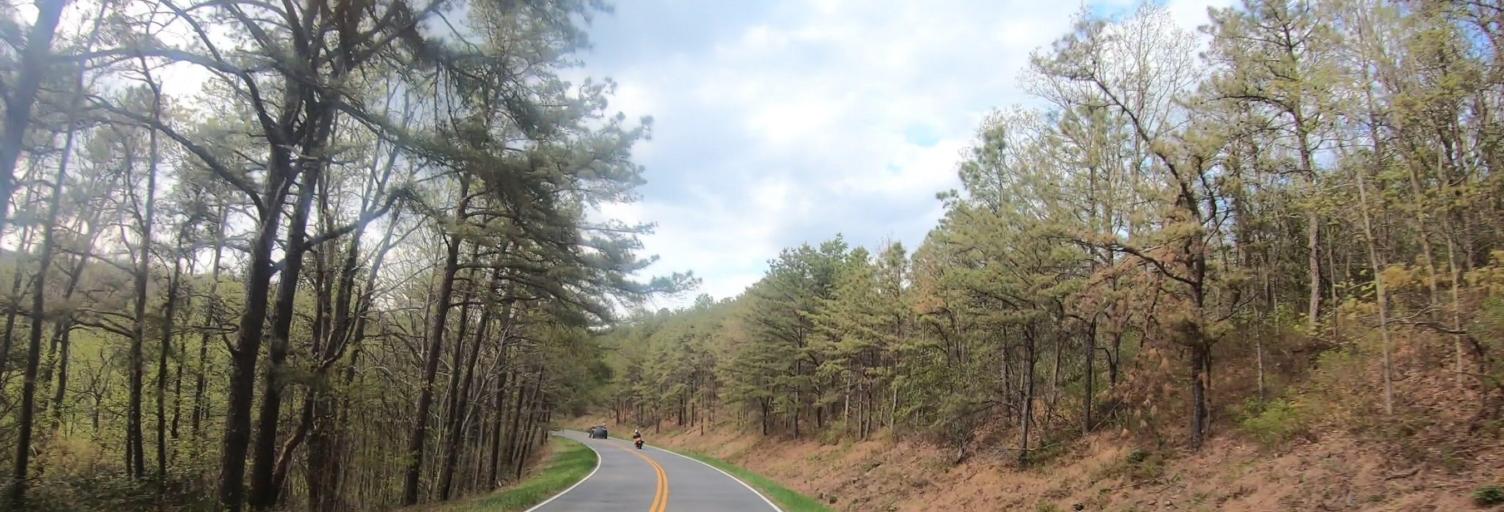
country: US
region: Virginia
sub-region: Augusta County
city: Dooms
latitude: 38.1114
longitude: -78.7824
